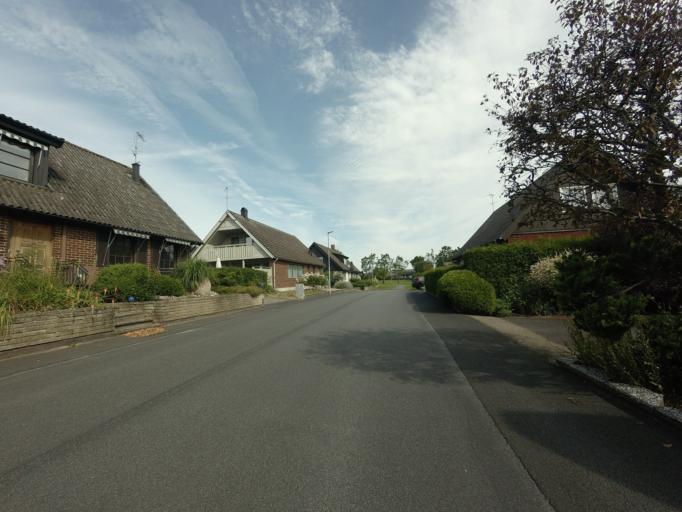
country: SE
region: Skane
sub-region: Simrishamns Kommun
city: Simrishamn
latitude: 55.5421
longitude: 14.3499
